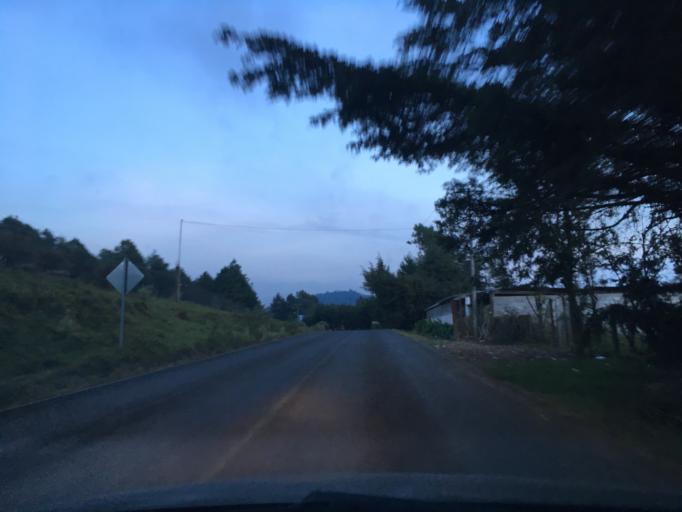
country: MX
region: Michoacan
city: Charapan
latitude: 19.6539
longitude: -102.2440
